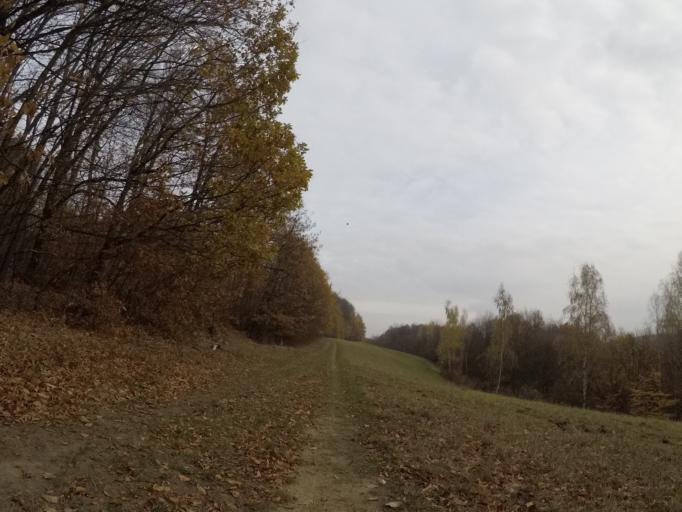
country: SK
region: Presovsky
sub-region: Okres Presov
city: Presov
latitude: 48.9416
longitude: 21.1404
